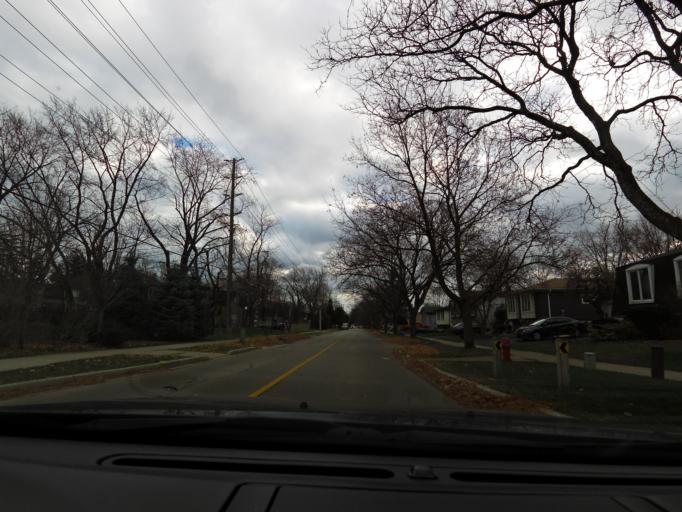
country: CA
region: Ontario
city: Burlington
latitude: 43.3174
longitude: -79.8181
